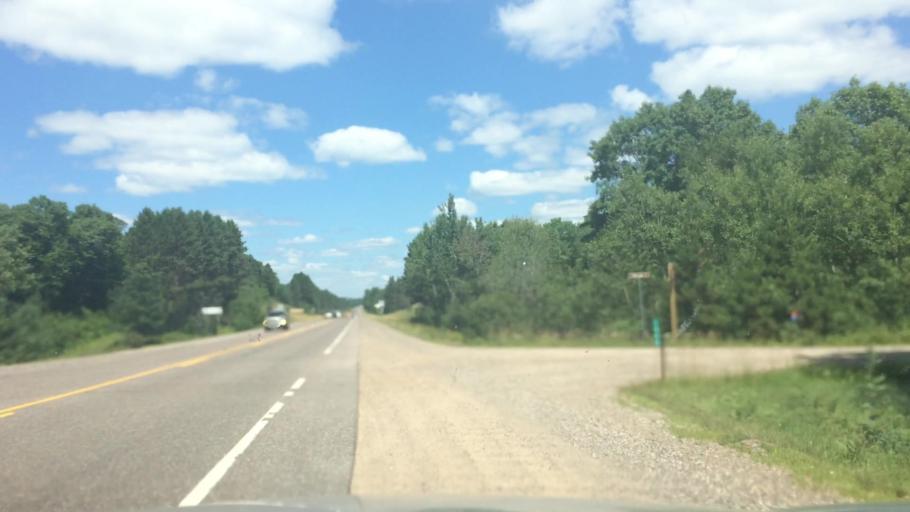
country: US
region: Wisconsin
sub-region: Vilas County
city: Lac du Flambeau
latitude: 45.9521
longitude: -89.7008
